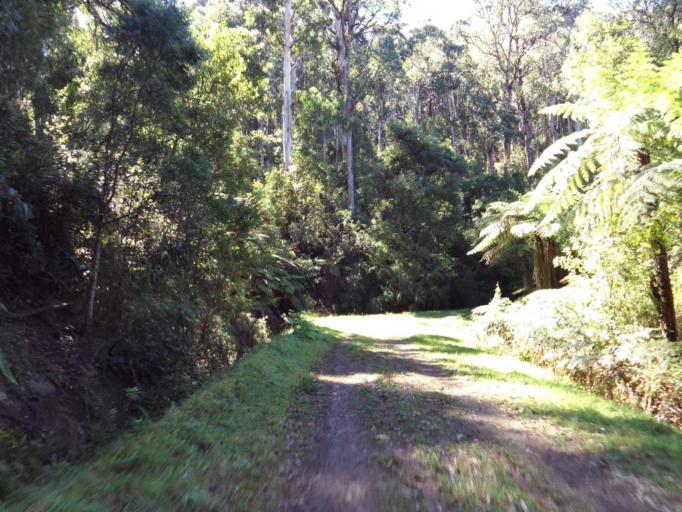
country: AU
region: Victoria
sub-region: Yarra Ranges
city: Launching Place
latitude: -37.7391
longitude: 145.5648
